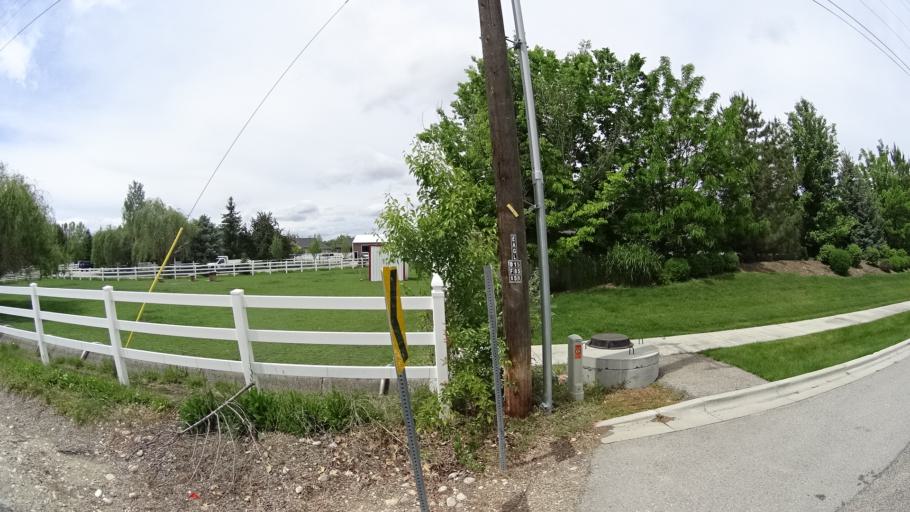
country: US
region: Idaho
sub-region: Ada County
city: Eagle
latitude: 43.7010
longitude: -116.4037
